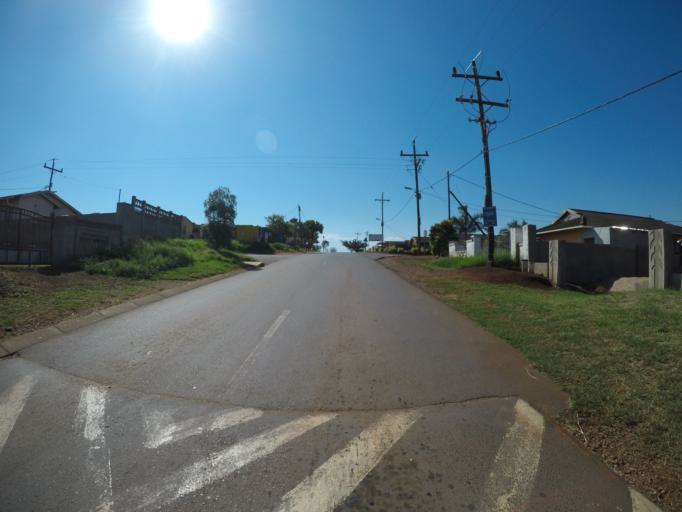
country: ZA
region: KwaZulu-Natal
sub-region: uThungulu District Municipality
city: Empangeni
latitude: -28.7737
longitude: 31.8813
